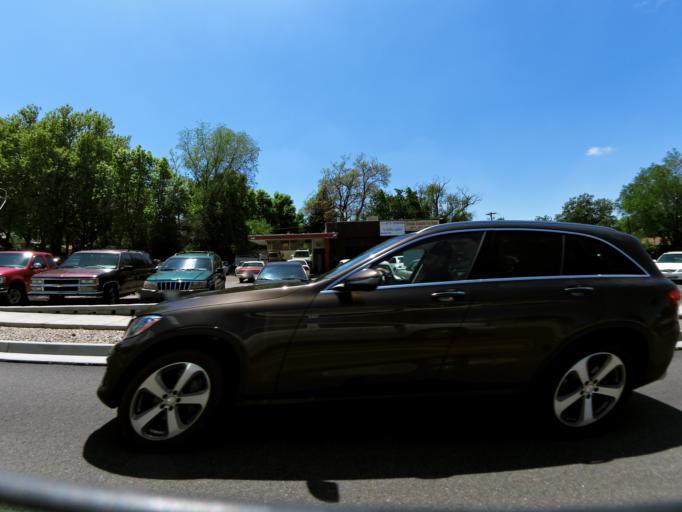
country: US
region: Utah
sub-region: Weber County
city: South Ogden
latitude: 41.1902
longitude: -111.9615
